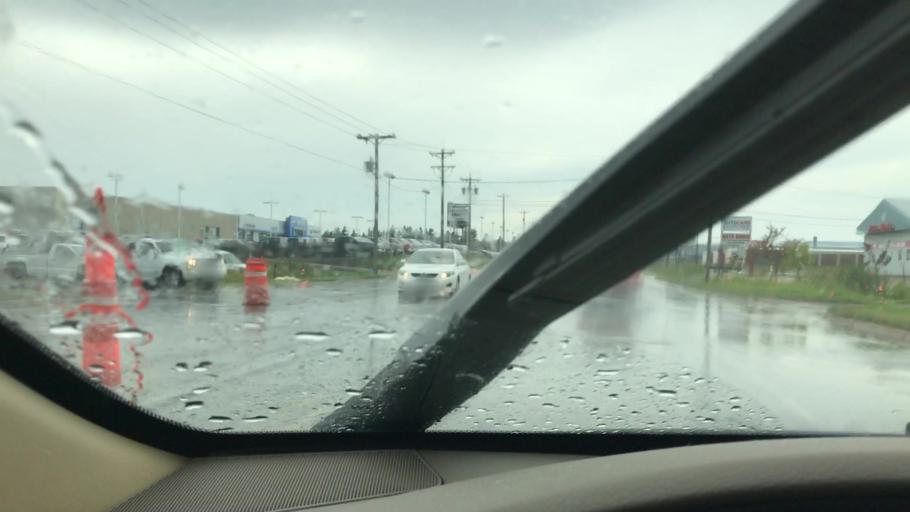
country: US
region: Minnesota
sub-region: Saint Louis County
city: Hermantown
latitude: 46.8221
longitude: -92.1801
